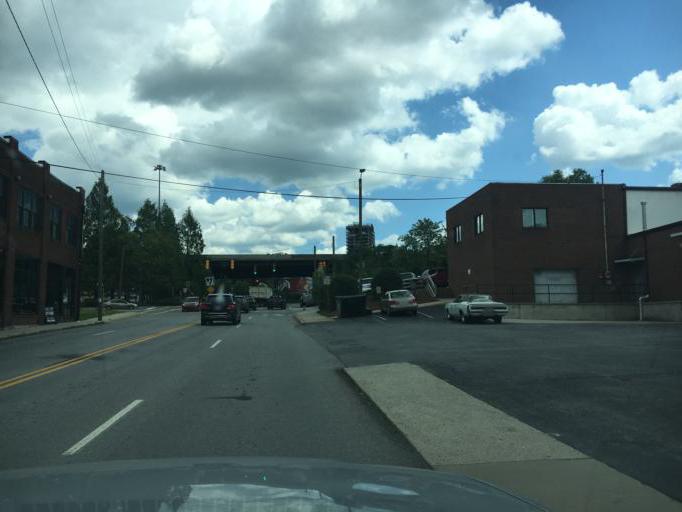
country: US
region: North Carolina
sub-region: Buncombe County
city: Asheville
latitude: 35.6003
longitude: -82.5550
